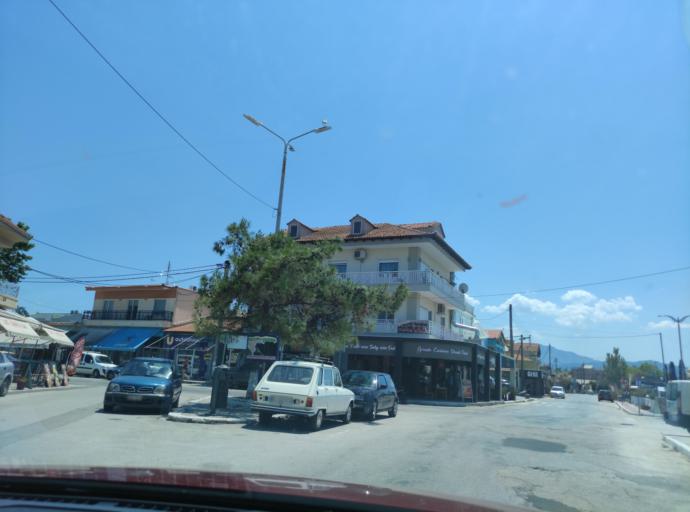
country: GR
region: East Macedonia and Thrace
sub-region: Nomos Kavalas
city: Keramoti
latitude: 40.8585
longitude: 24.7037
